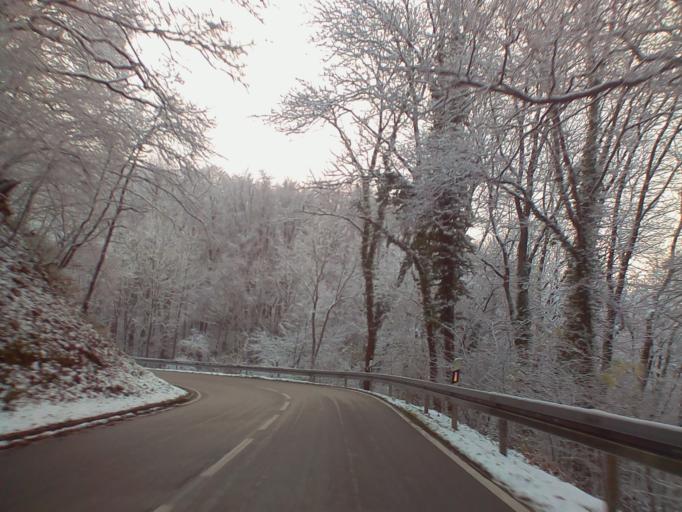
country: DE
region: Hesse
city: Unter-Abtsteinach
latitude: 49.5296
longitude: 8.7683
